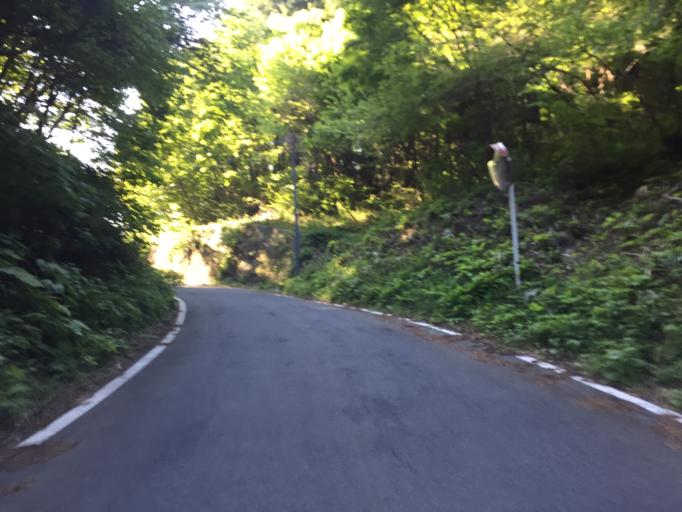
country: JP
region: Ibaraki
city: Kitaibaraki
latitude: 36.9024
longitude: 140.5938
